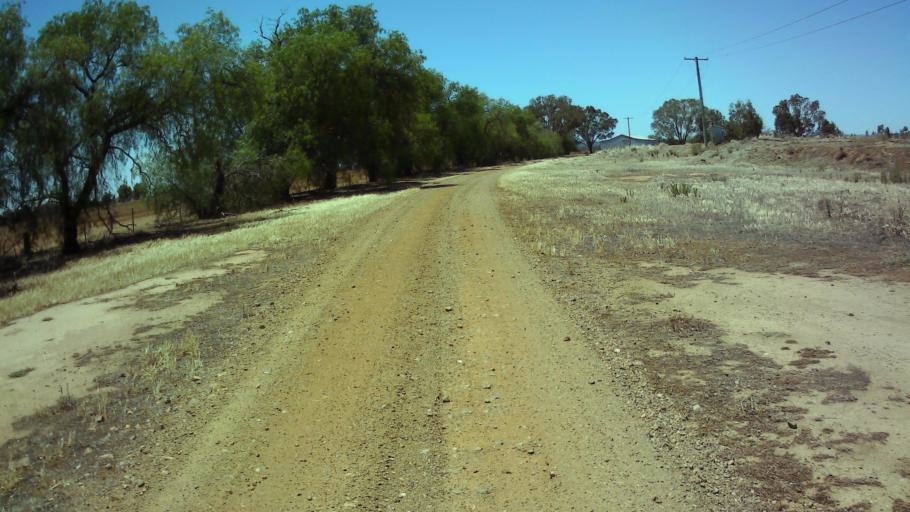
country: AU
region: New South Wales
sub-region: Weddin
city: Grenfell
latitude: -33.7335
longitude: 148.0969
